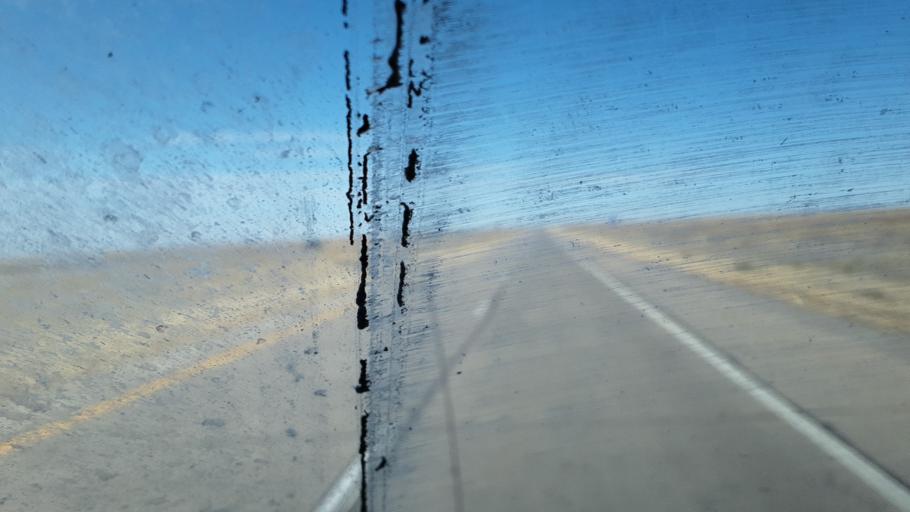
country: US
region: Colorado
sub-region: Weld County
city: Keenesburg
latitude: 40.1847
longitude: -104.3037
